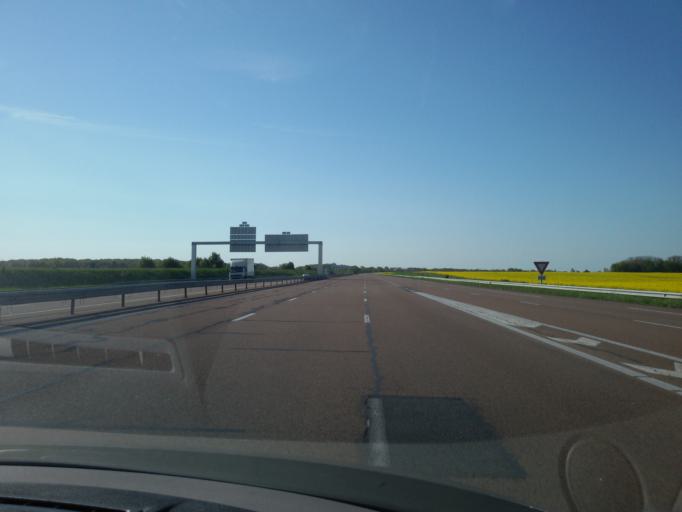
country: FR
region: Centre
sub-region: Departement du Loiret
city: Courtenay
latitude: 48.0412
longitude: 3.1182
